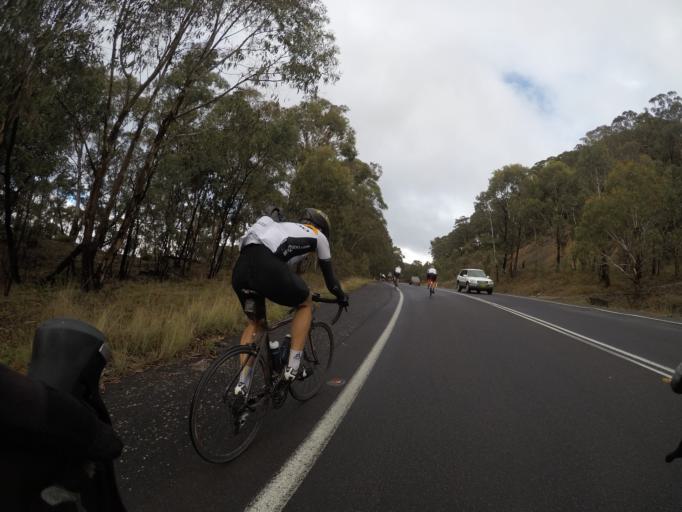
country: AU
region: New South Wales
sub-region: Lithgow
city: Lithgow
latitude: -33.5060
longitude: 150.1795
